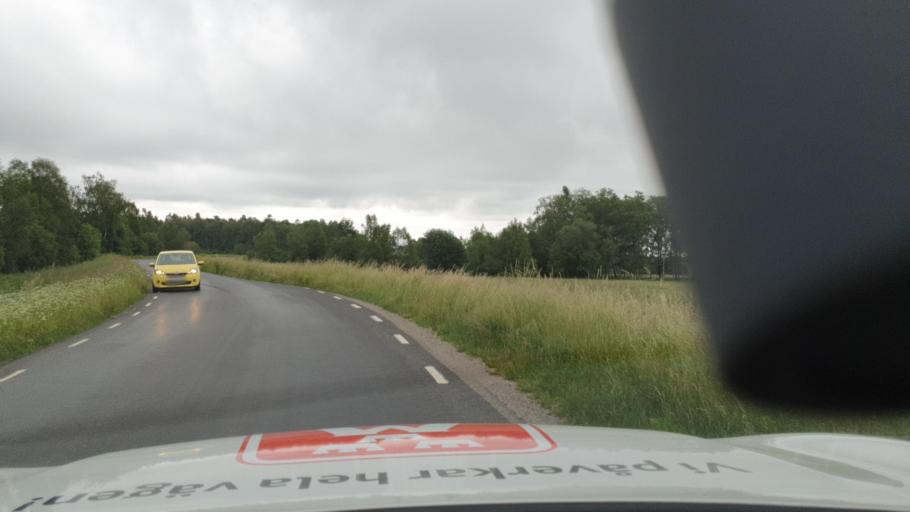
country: SE
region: Vaestra Goetaland
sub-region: Falkopings Kommun
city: Falkoeping
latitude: 58.0784
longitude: 13.6360
